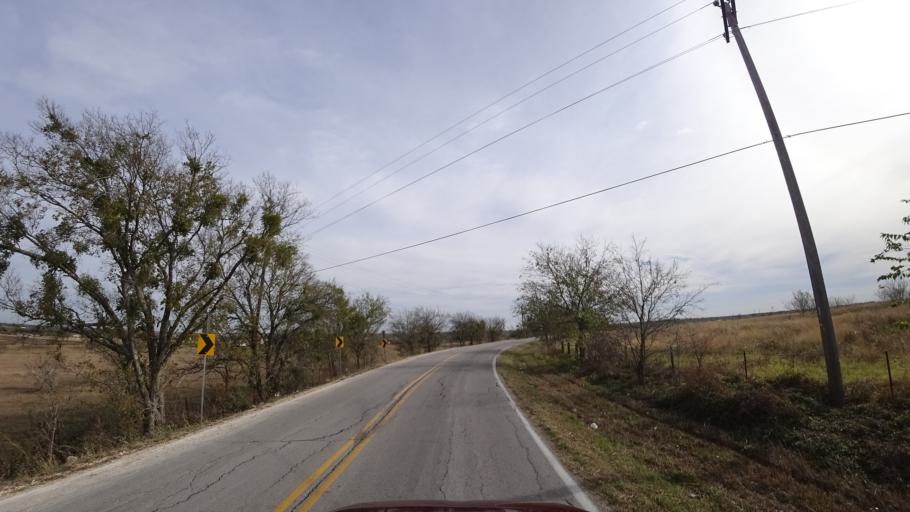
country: US
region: Texas
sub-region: Travis County
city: Garfield
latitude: 30.1279
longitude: -97.6014
